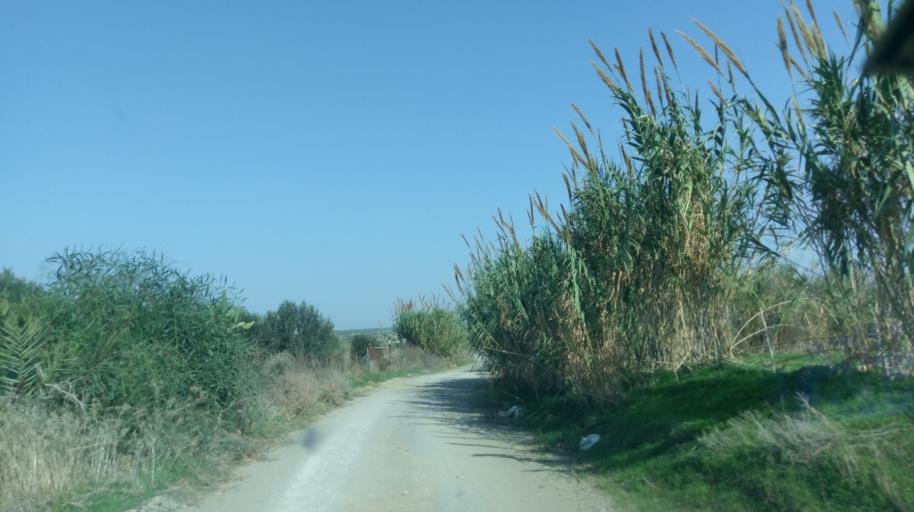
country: CY
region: Lefkosia
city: Morfou
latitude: 35.2910
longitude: 32.9500
